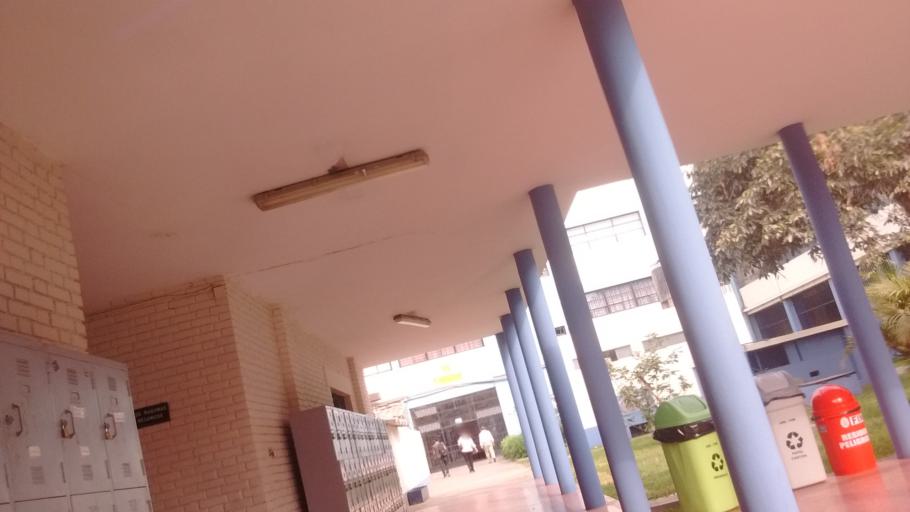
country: PE
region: Lima
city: Lima
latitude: -12.0241
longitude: -77.0473
